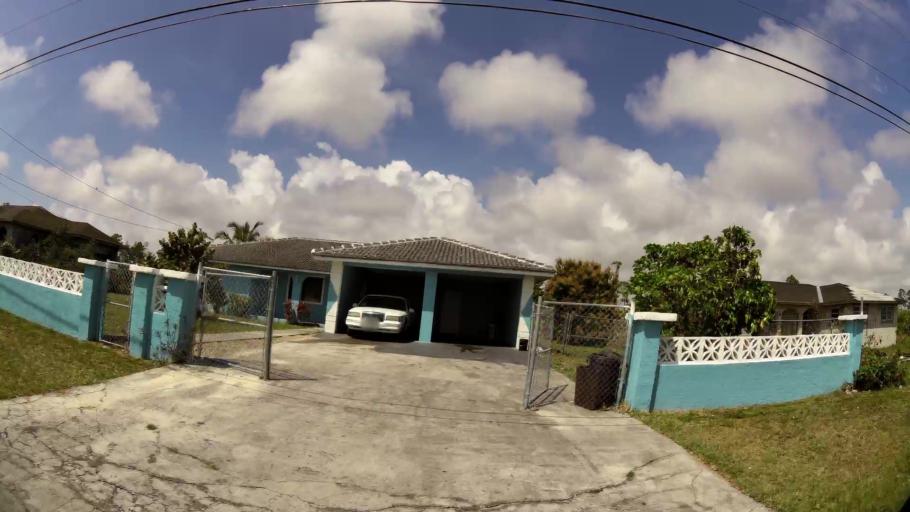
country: BS
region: Freeport
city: Freeport
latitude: 26.5031
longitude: -78.7237
